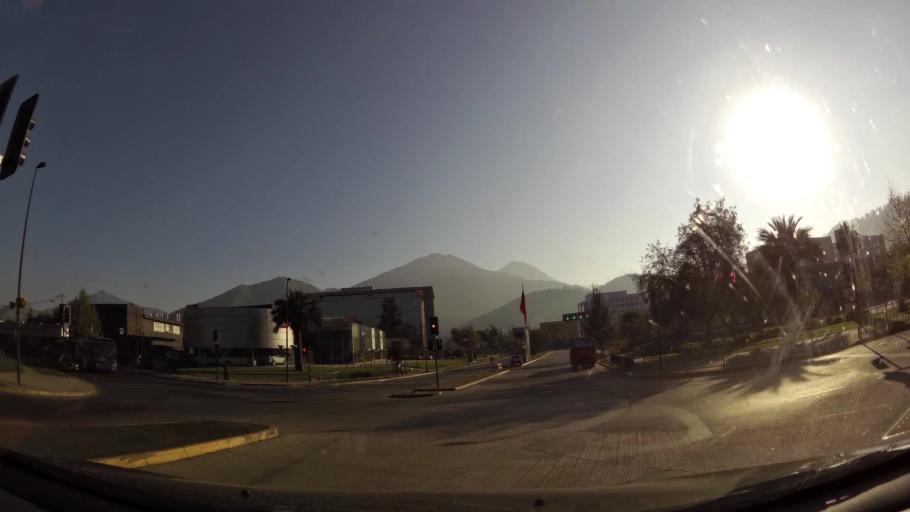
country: CL
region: Santiago Metropolitan
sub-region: Provincia de Santiago
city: Santiago
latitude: -33.3944
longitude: -70.6213
